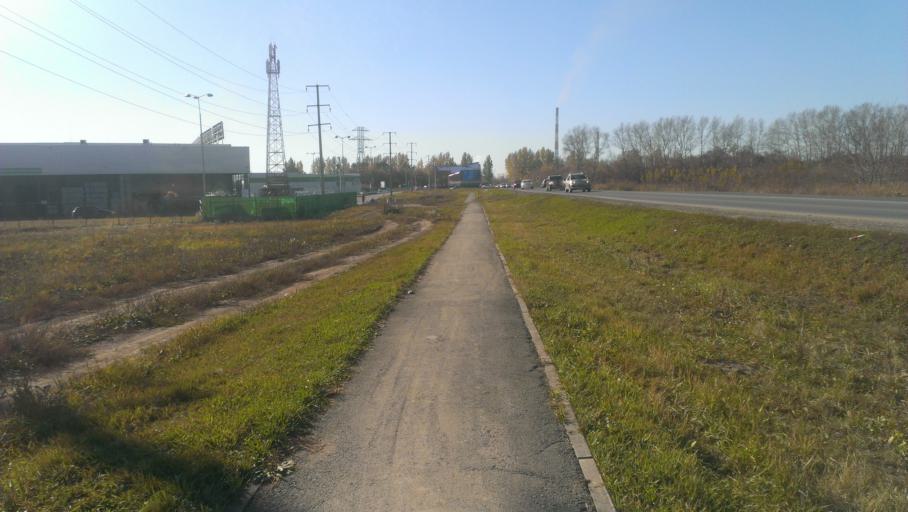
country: RU
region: Altai Krai
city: Novosilikatnyy
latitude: 53.3520
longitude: 83.6320
